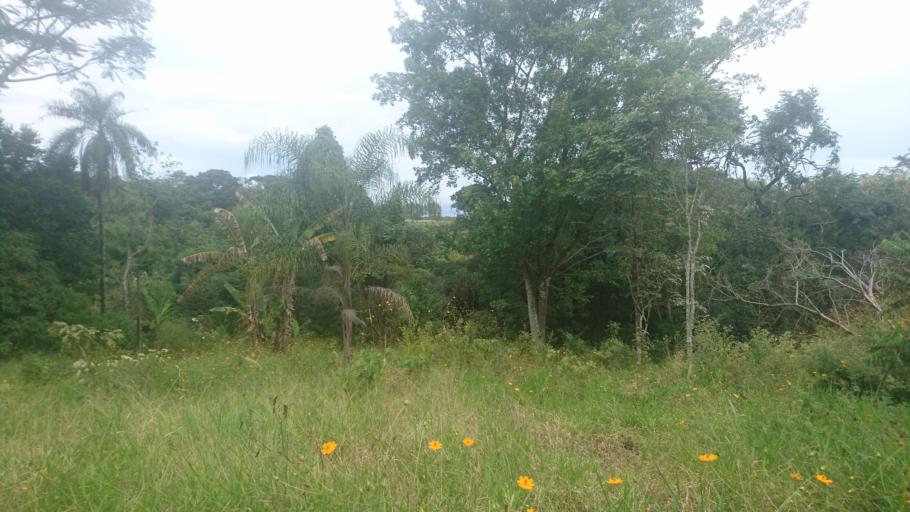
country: BR
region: Sao Paulo
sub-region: Casa Branca
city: Casa Branca
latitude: -21.7852
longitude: -47.0785
